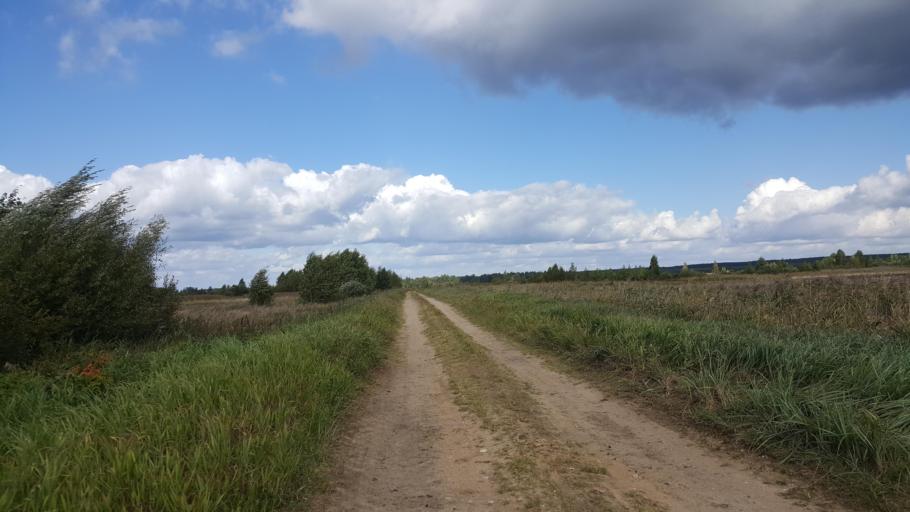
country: BY
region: Brest
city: Kamyanyets
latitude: 52.4531
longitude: 23.9346
